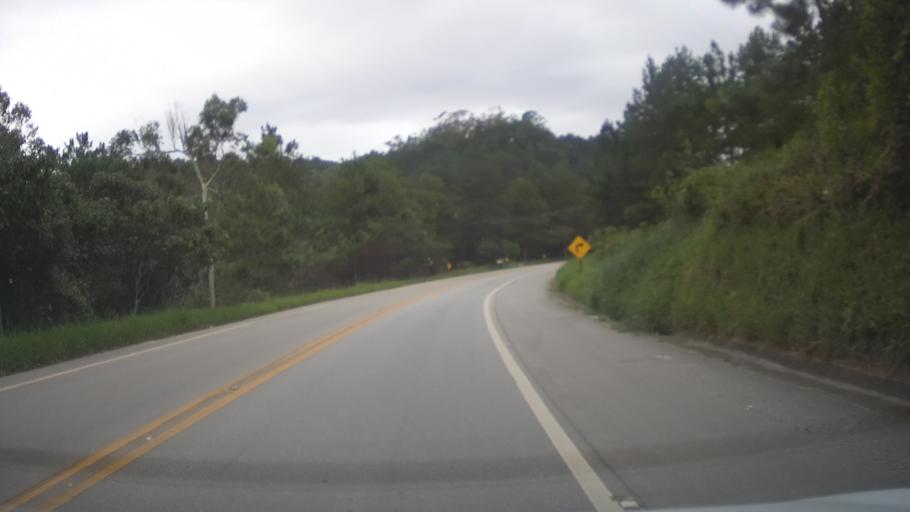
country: BR
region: Sao Paulo
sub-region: Aruja
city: Aruja
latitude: -23.3574
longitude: -46.4216
